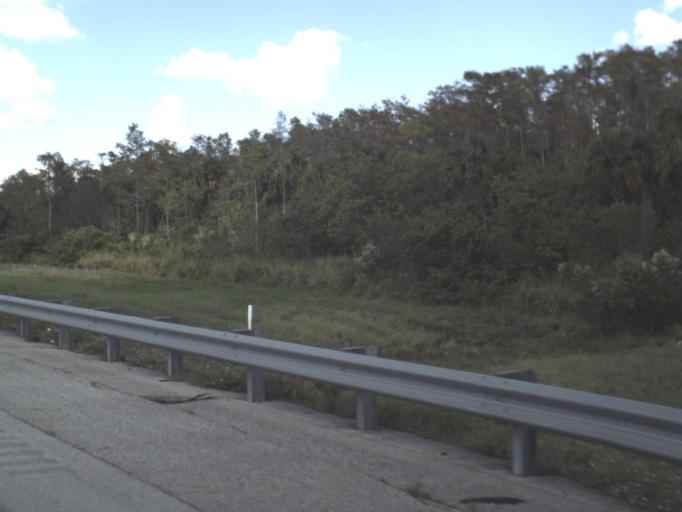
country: US
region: Florida
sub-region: Indian River County
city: West Vero Corridor
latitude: 27.5545
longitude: -80.6389
